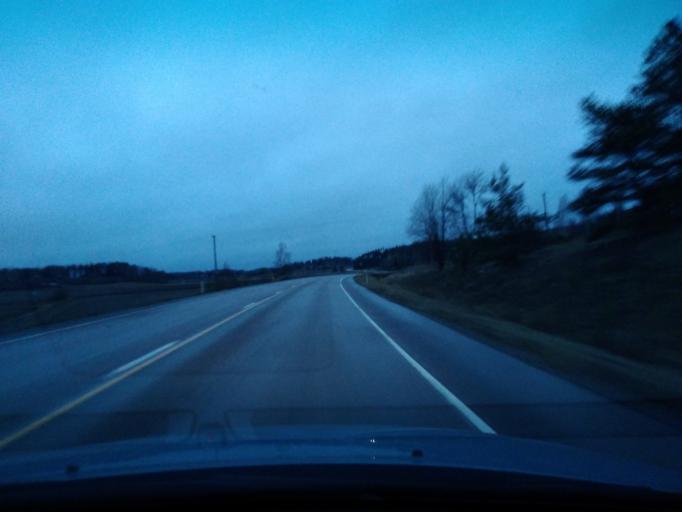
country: FI
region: Uusimaa
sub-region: Porvoo
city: Askola
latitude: 60.4782
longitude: 25.5658
